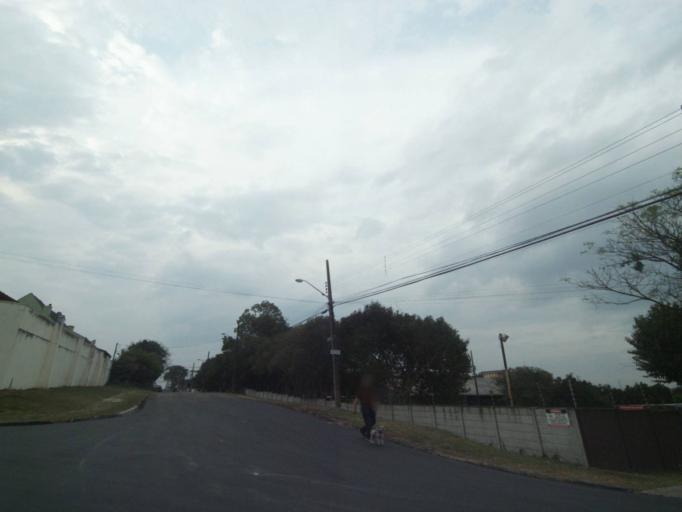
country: BR
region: Parana
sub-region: Pinhais
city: Pinhais
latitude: -25.4735
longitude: -49.2303
